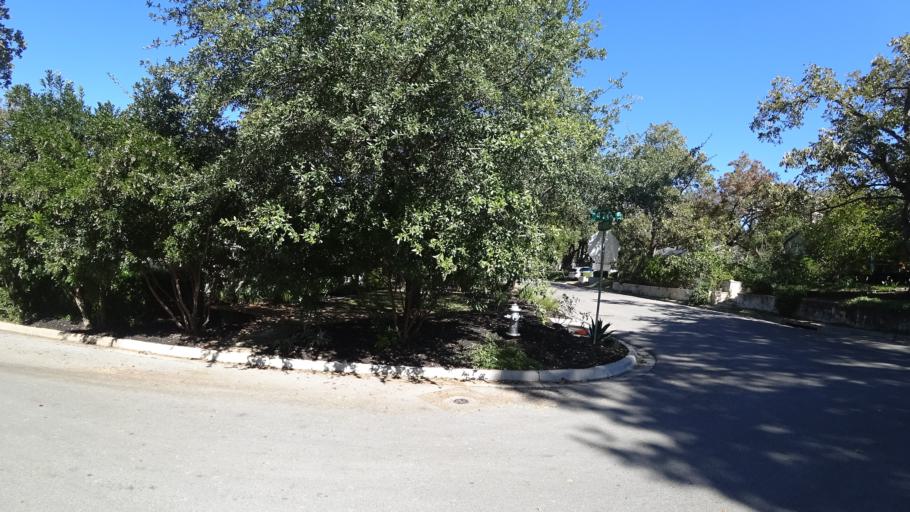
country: US
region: Texas
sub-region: Travis County
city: Austin
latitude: 30.3198
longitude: -97.7435
